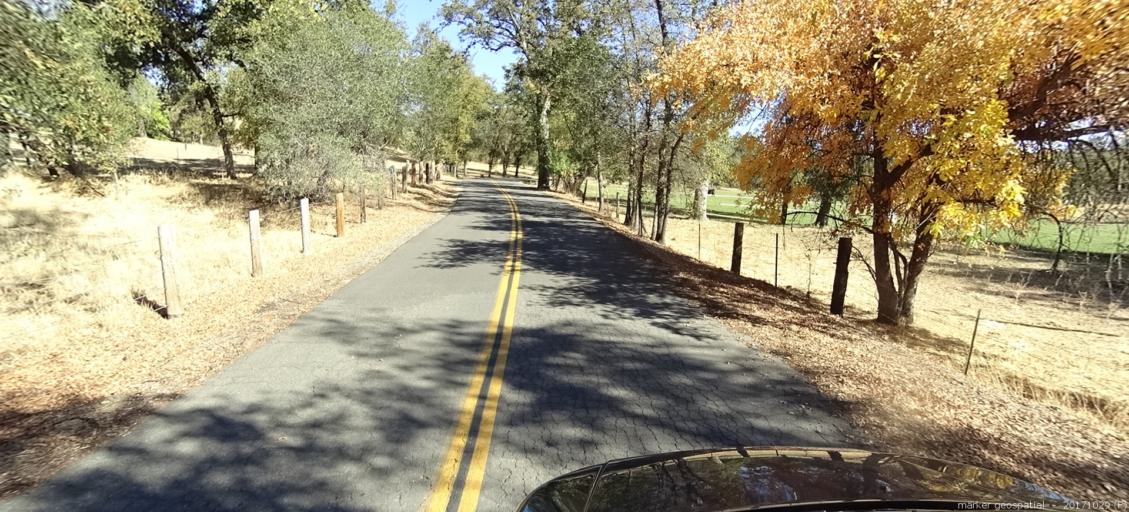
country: US
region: California
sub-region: Shasta County
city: Shasta
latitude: 40.4828
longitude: -122.6596
